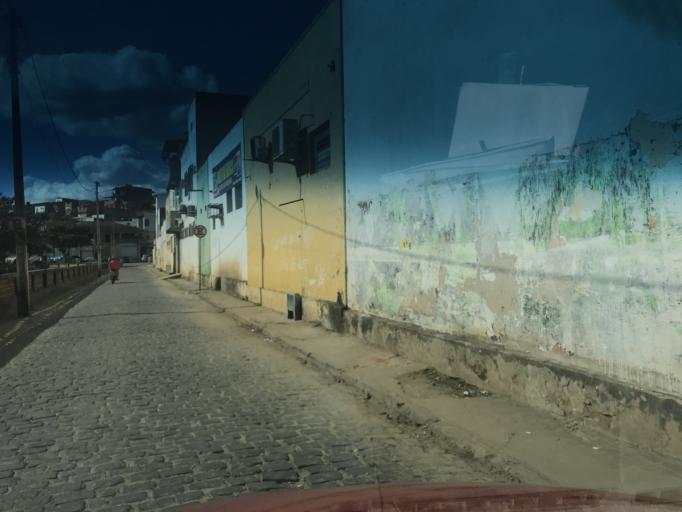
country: BR
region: Bahia
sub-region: Gandu
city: Gandu
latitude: -13.7452
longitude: -39.4888
